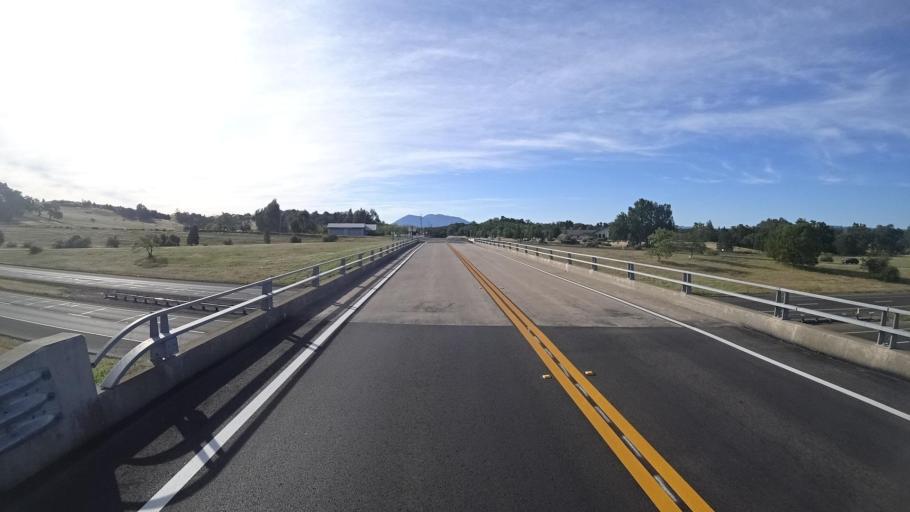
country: US
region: California
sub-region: Lake County
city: North Lakeport
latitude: 39.0843
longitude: -122.9264
